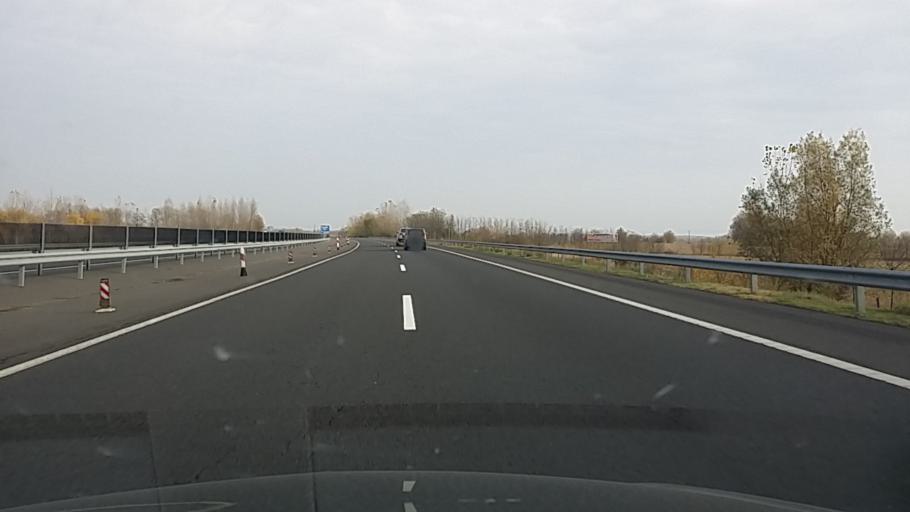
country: HU
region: Szabolcs-Szatmar-Bereg
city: Kalmanhaza
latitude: 47.8959
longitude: 21.6117
